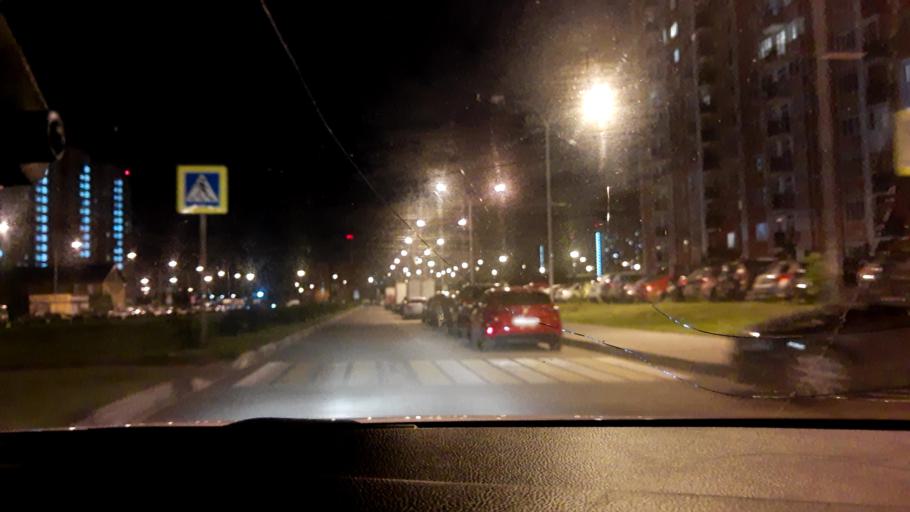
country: RU
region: Moskovskaya
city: Lesnoy Gorodok
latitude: 55.6579
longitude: 37.2311
